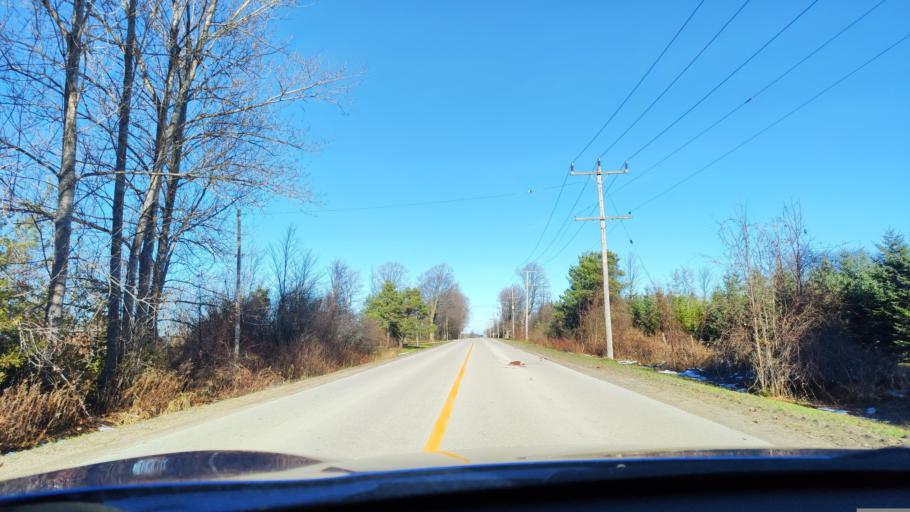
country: CA
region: Ontario
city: Collingwood
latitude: 44.4740
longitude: -80.1758
